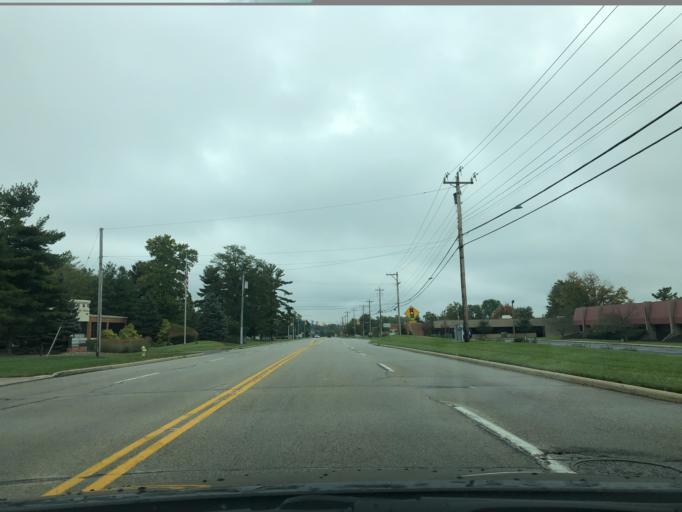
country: US
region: Ohio
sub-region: Hamilton County
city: Highpoint
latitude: 39.2802
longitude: -84.3526
